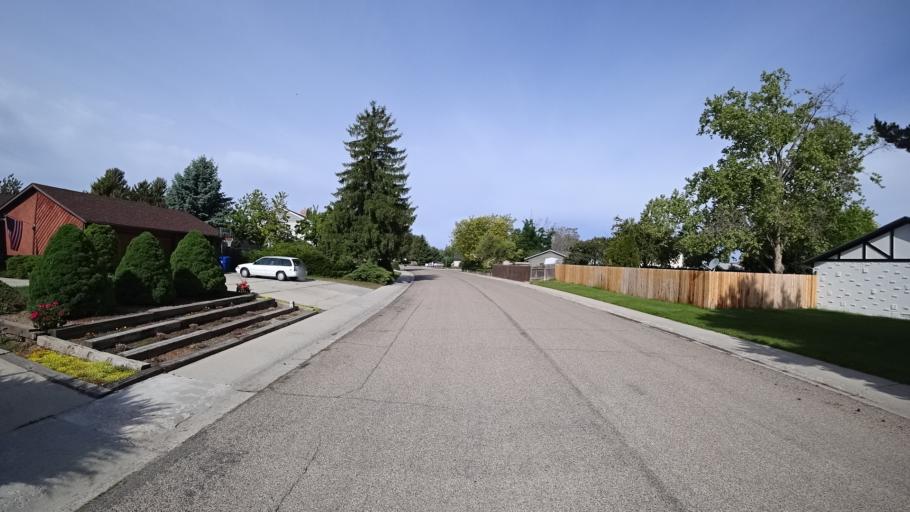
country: US
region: Idaho
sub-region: Ada County
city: Meridian
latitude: 43.5662
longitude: -116.3275
